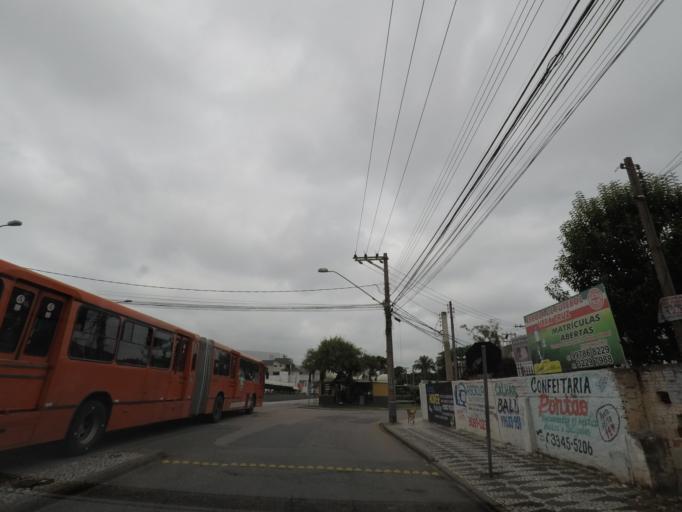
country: BR
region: Parana
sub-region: Curitiba
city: Curitiba
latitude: -25.4756
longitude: -49.2930
